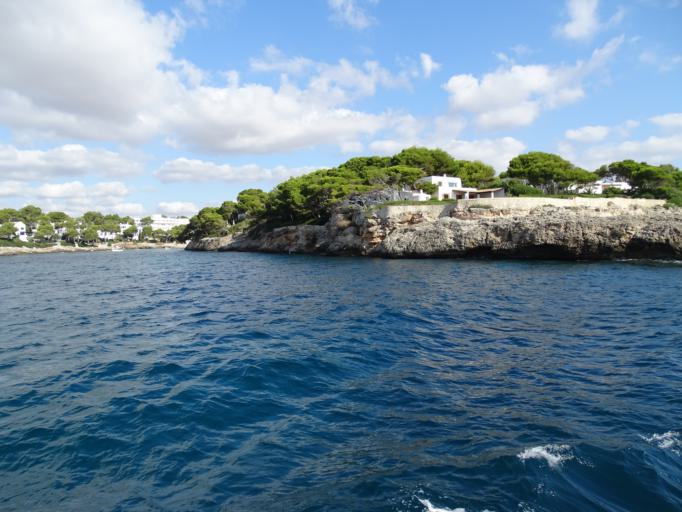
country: ES
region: Balearic Islands
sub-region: Illes Balears
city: Santanyi
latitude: 39.3686
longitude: 3.2332
